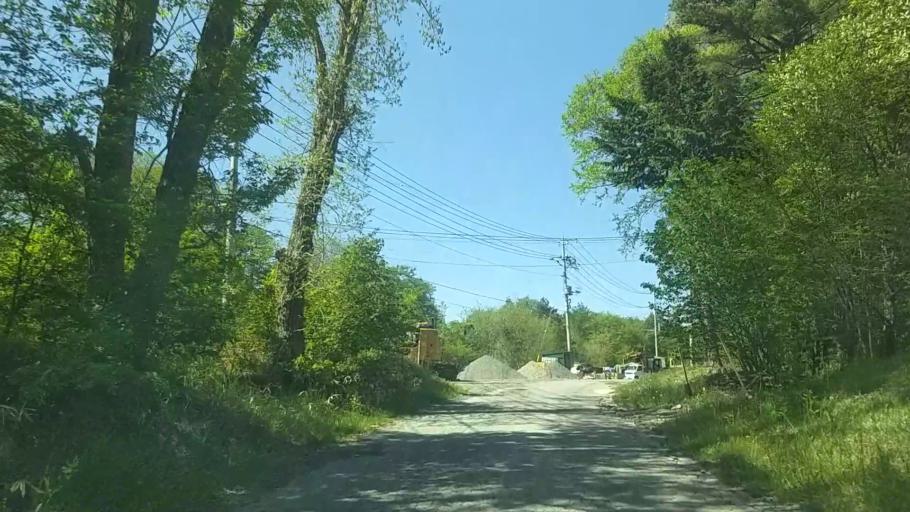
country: JP
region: Yamanashi
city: Nirasaki
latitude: 35.9161
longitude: 138.4329
